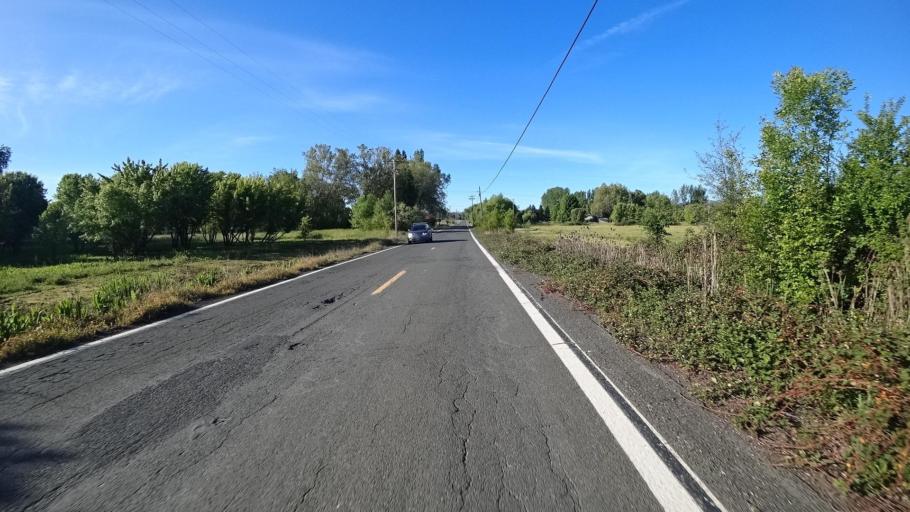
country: US
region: California
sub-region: Lake County
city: North Lakeport
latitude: 39.0845
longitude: -122.9498
